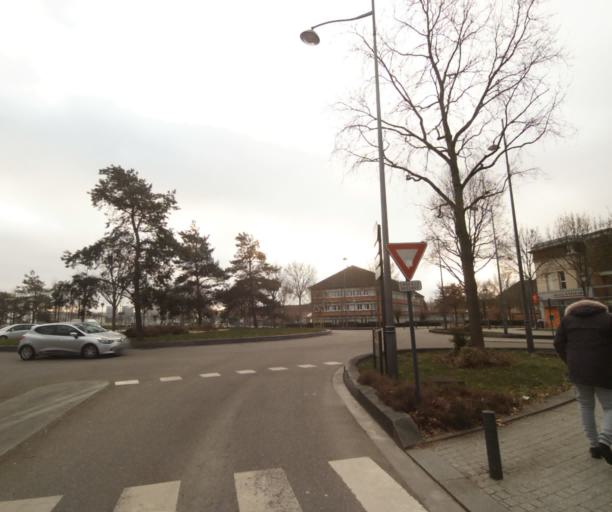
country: FR
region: Champagne-Ardenne
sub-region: Departement de la Haute-Marne
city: Bettancourt-la-Ferree
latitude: 48.6445
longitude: 4.9633
